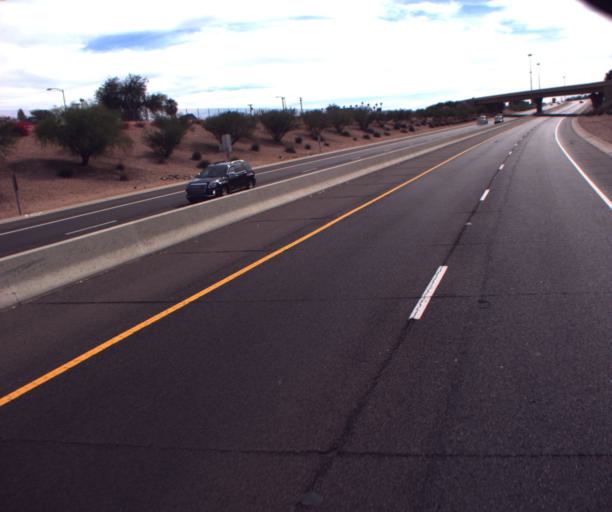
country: US
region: Arizona
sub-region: Maricopa County
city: Tempe Junction
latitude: 33.4562
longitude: -111.9828
